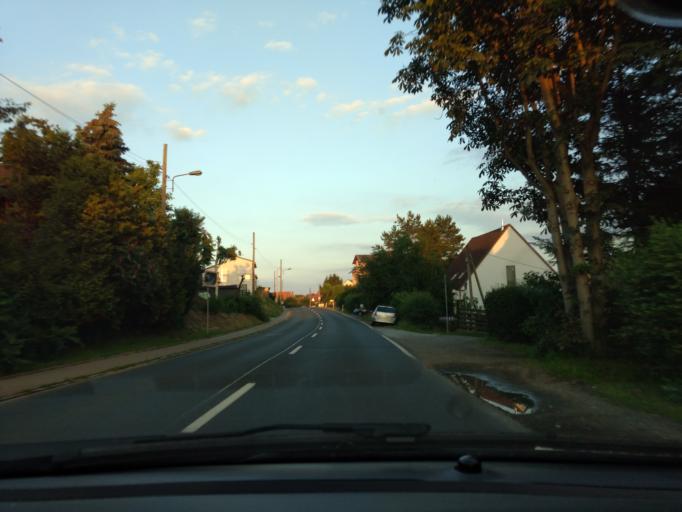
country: DE
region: Saxony
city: Radebeul
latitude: 51.1194
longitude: 13.6932
